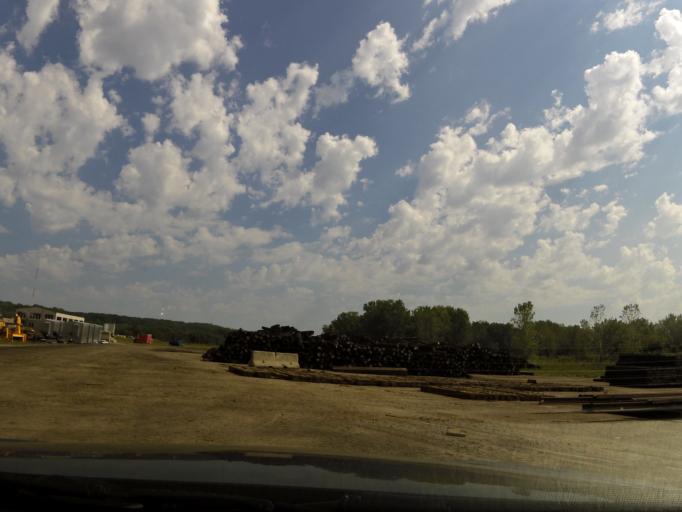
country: US
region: Minnesota
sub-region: Ramsey County
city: Saint Paul
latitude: 44.9379
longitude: -93.0470
